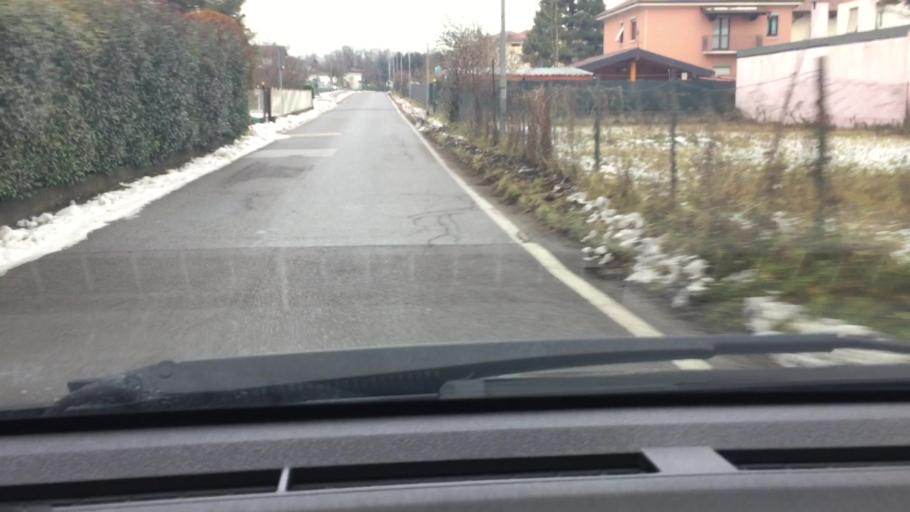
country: IT
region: Lombardy
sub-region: Provincia di Como
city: Gaggino
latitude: 45.8021
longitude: 8.9647
